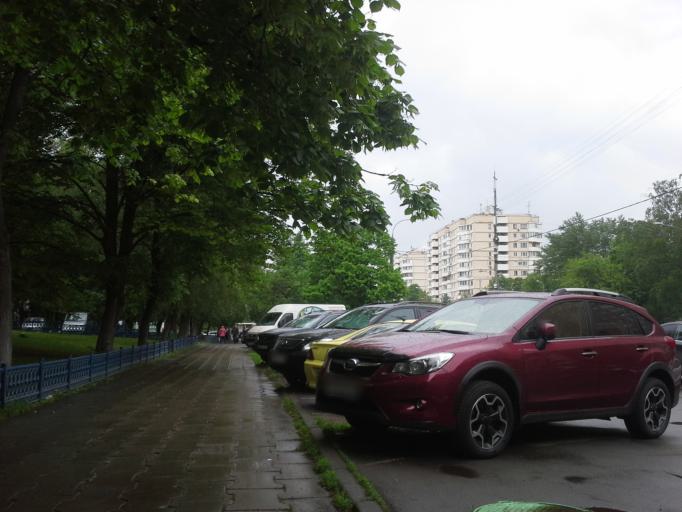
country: RU
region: Moscow
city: Kotlovka
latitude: 55.6520
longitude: 37.6051
